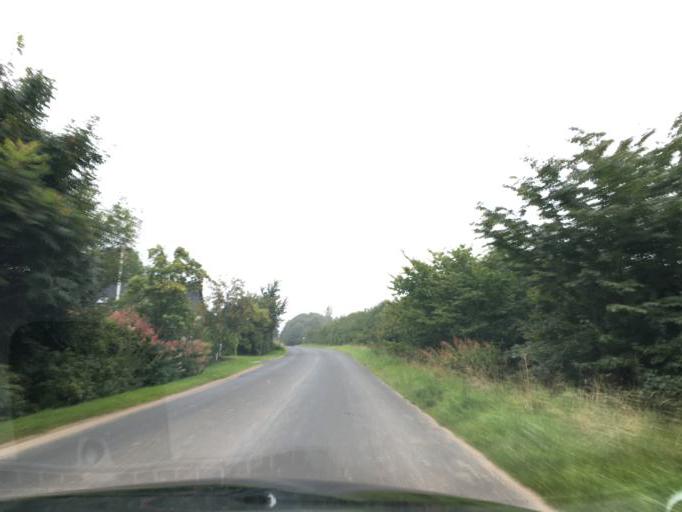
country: DK
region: South Denmark
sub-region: Kolding Kommune
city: Kolding
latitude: 55.5623
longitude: 9.4414
